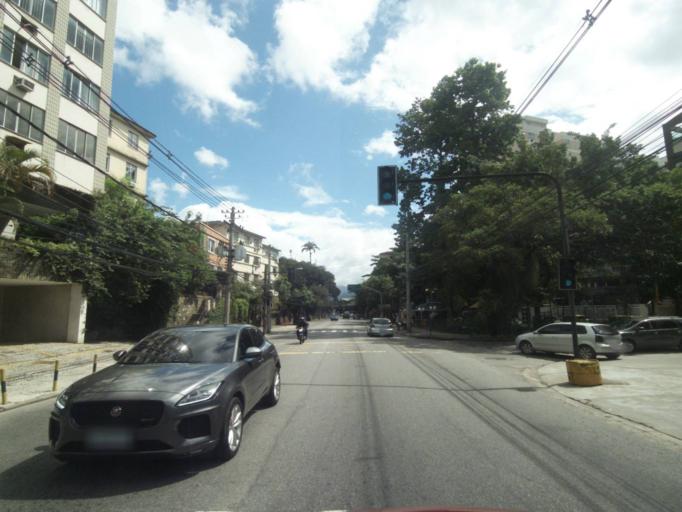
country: BR
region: Rio de Janeiro
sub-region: Sao Joao De Meriti
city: Sao Joao de Meriti
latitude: -22.9386
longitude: -43.3462
